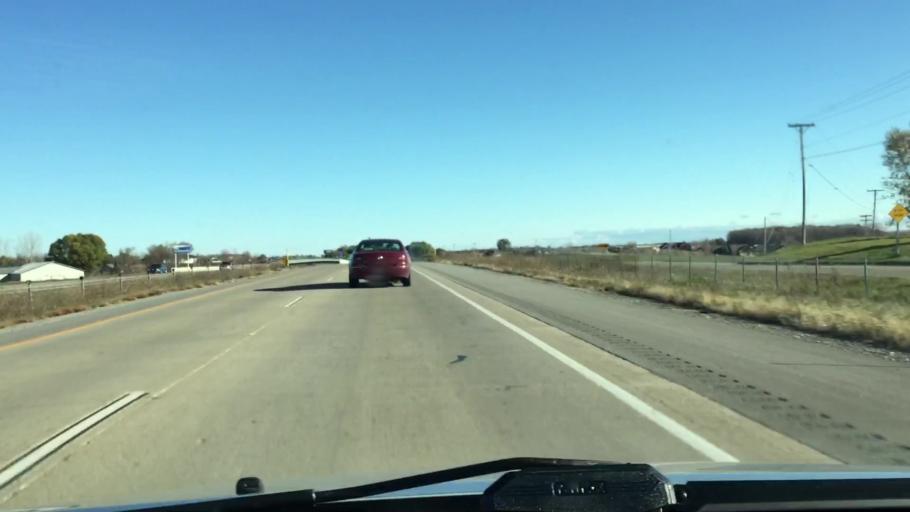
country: US
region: Wisconsin
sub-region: Brown County
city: Wrightstown
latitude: 44.3273
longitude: -88.2117
